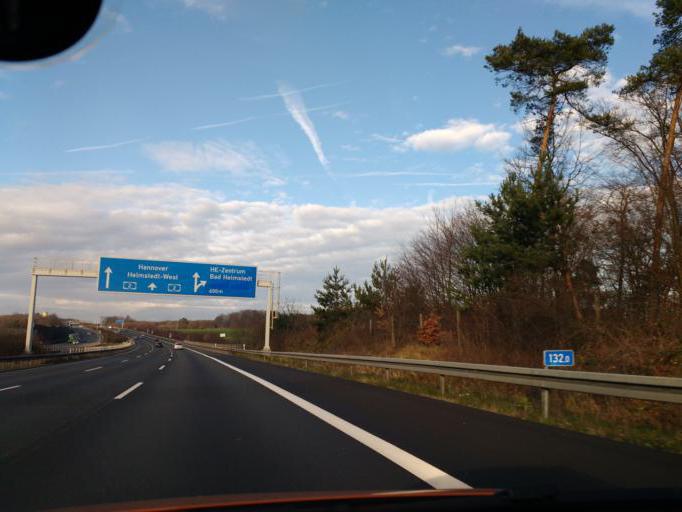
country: DE
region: Lower Saxony
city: Helmstedt
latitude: 52.2380
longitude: 11.0188
